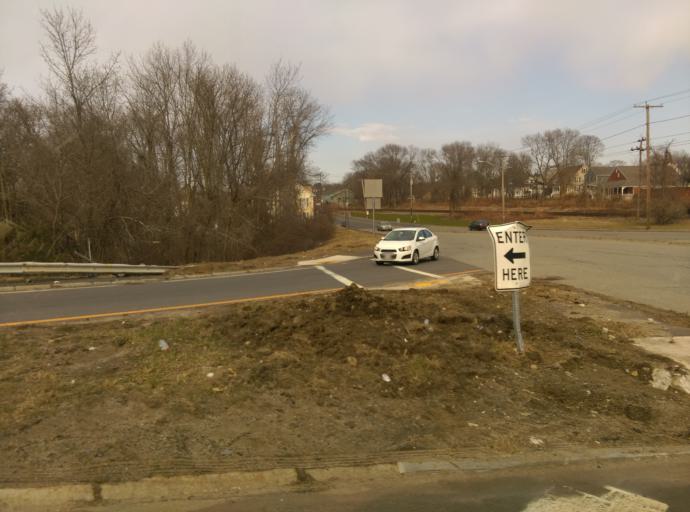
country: US
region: Massachusetts
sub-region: Essex County
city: North Andover
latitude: 42.7042
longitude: -71.1384
